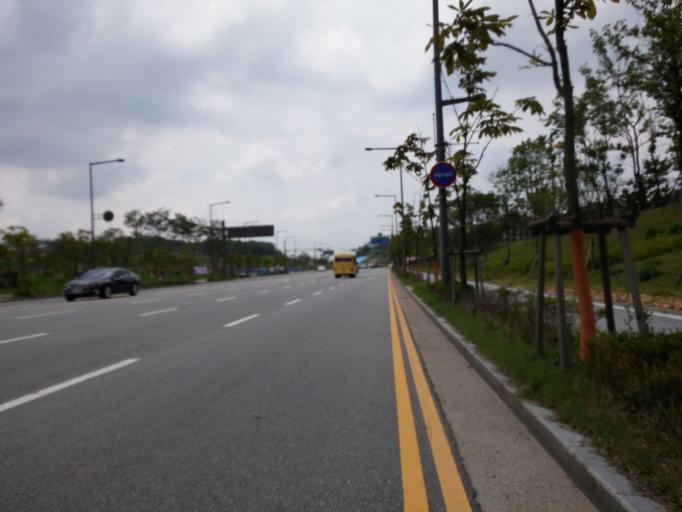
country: KR
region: Chungcheongnam-do
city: Gongju
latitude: 36.4999
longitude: 127.2382
